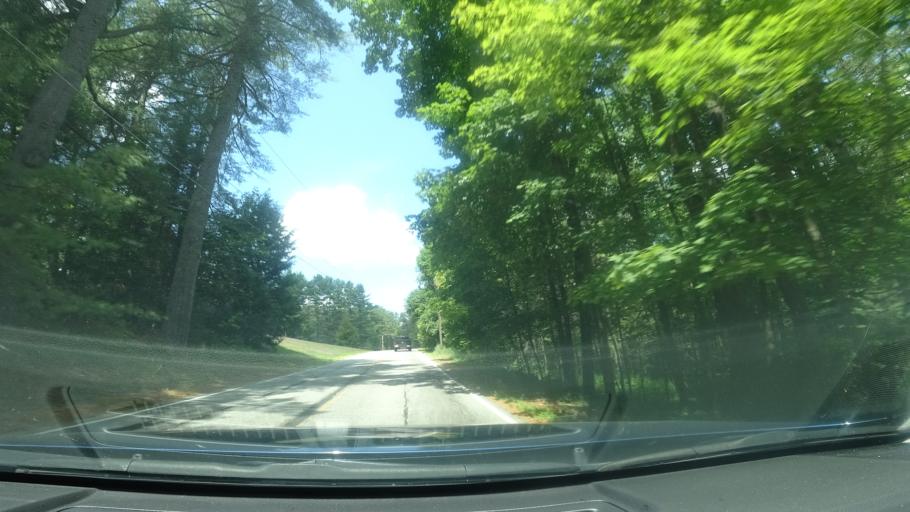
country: US
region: New York
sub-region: Warren County
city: Warrensburg
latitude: 43.6616
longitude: -73.8352
